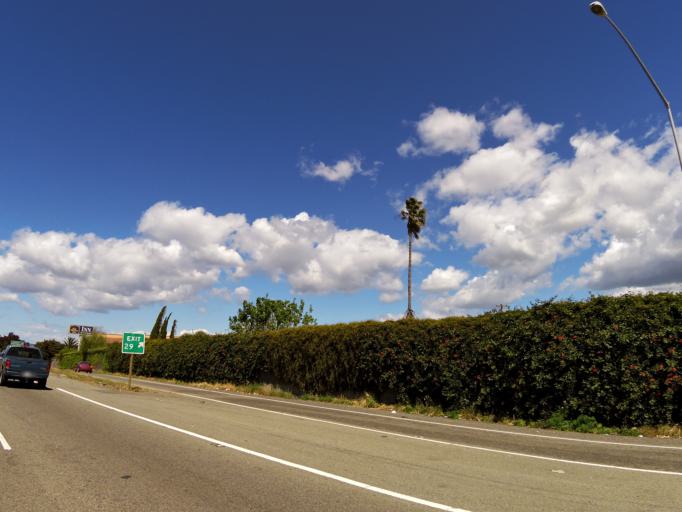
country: US
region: California
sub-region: Alameda County
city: Cherryland
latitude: 37.6642
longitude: -122.1062
